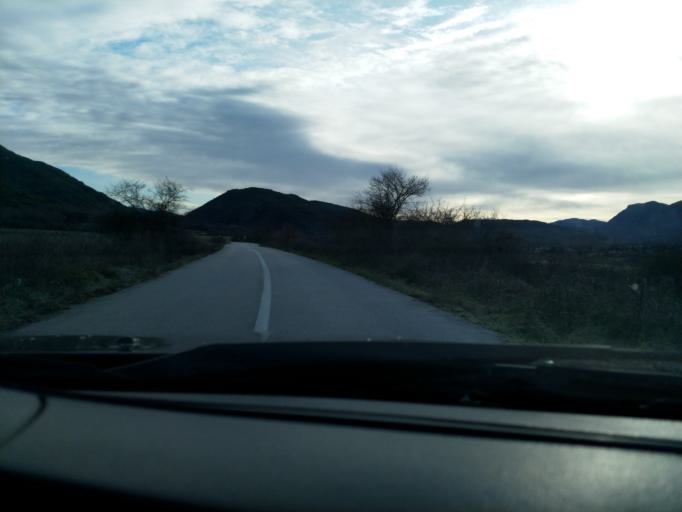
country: GR
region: Epirus
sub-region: Nomos Ioanninon
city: Asprangeloi
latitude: 39.8686
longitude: 20.7075
